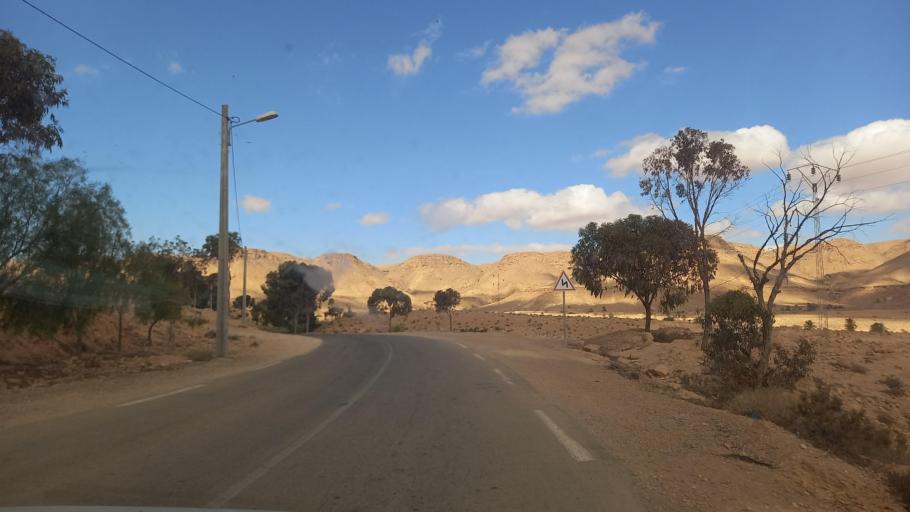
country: TN
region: Tataouine
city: Tataouine
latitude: 32.9159
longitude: 10.2766
